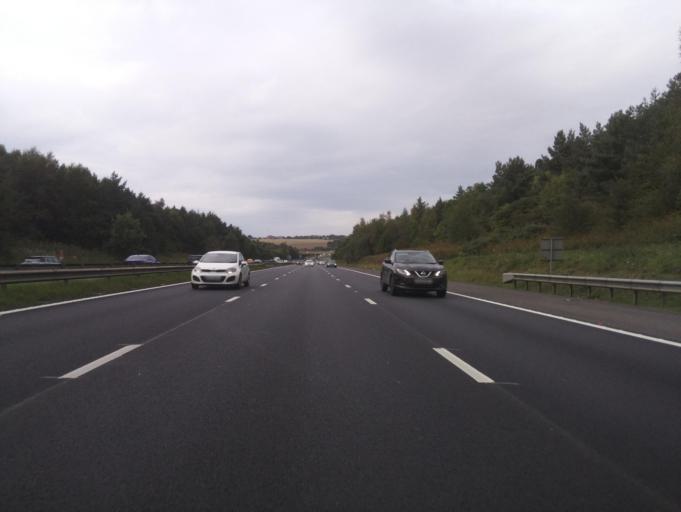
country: GB
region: England
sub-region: County Durham
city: Durham
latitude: 54.7615
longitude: -1.5279
